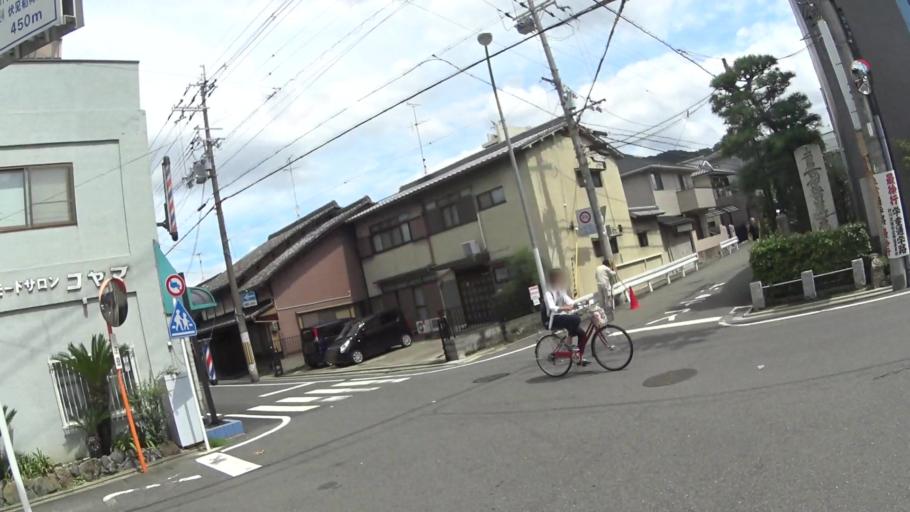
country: JP
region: Kyoto
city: Kyoto
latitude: 34.9629
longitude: 135.7709
